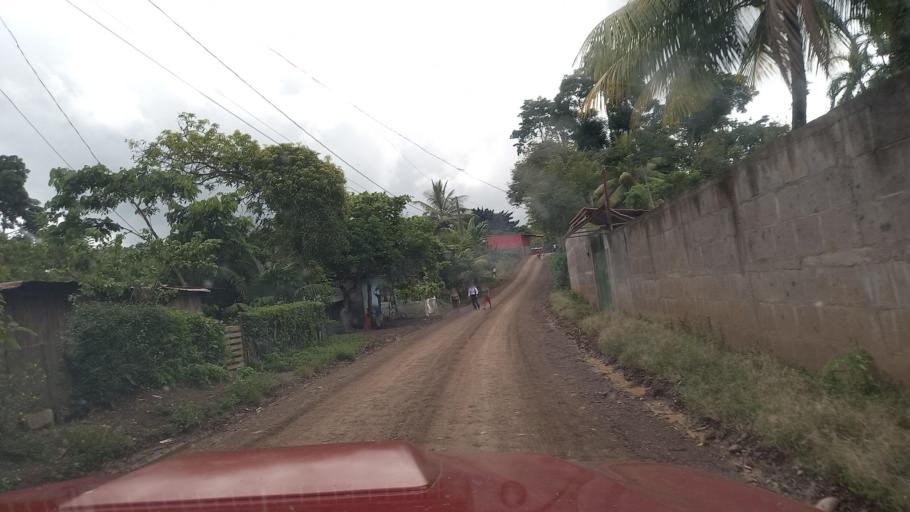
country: NI
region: Jinotega
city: San Jose de Bocay
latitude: 13.3480
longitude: -85.6584
